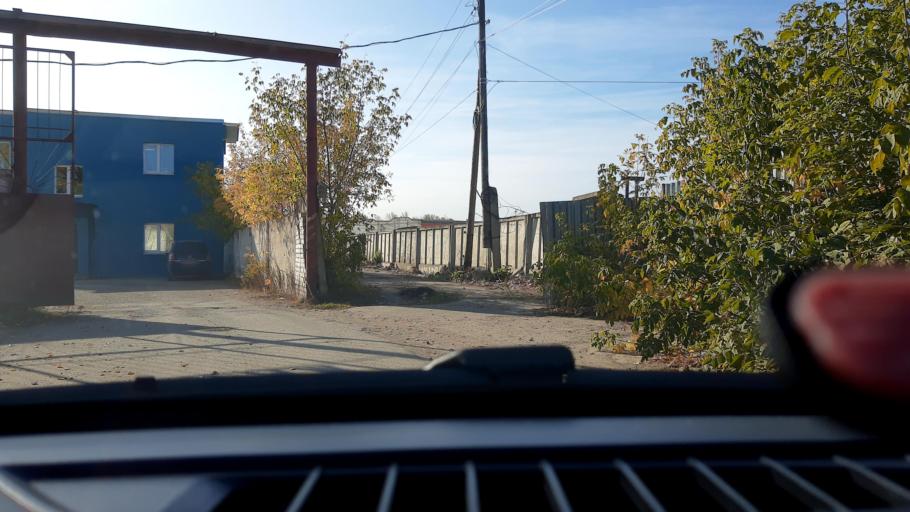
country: RU
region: Nizjnij Novgorod
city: Nizhniy Novgorod
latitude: 56.3035
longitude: 43.8893
